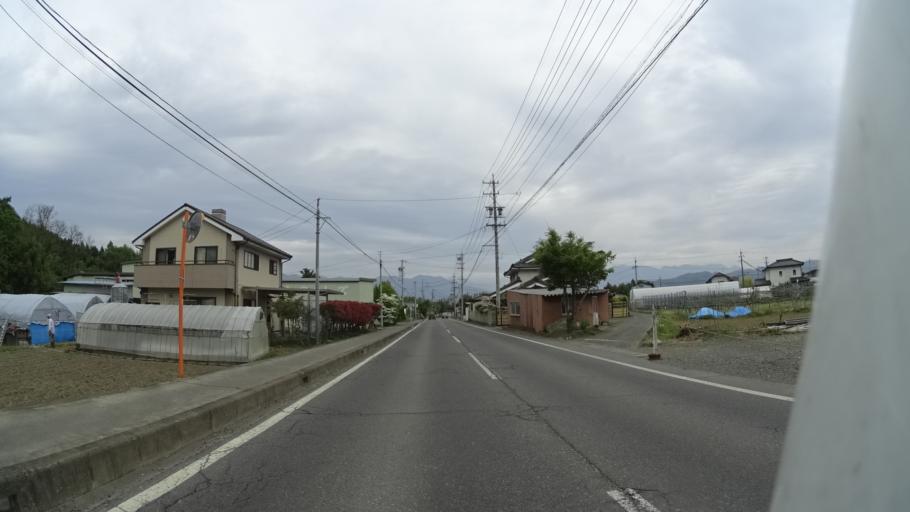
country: JP
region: Nagano
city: Kamimaruko
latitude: 36.3675
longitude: 138.1868
